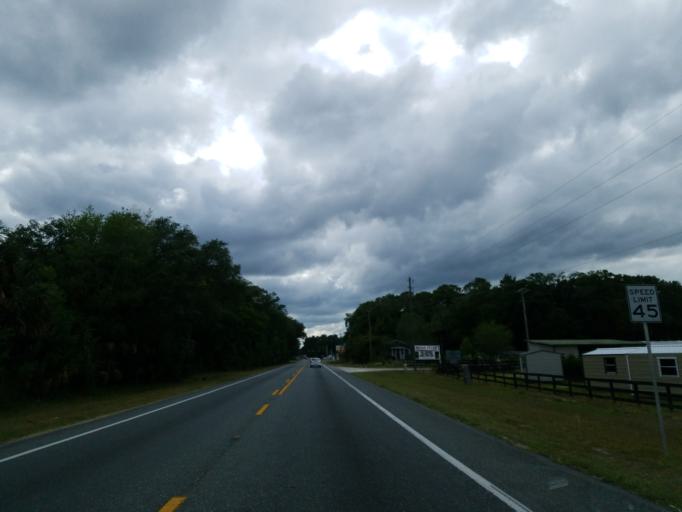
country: US
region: Florida
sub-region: Marion County
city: Ocala
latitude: 29.2595
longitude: -82.1100
